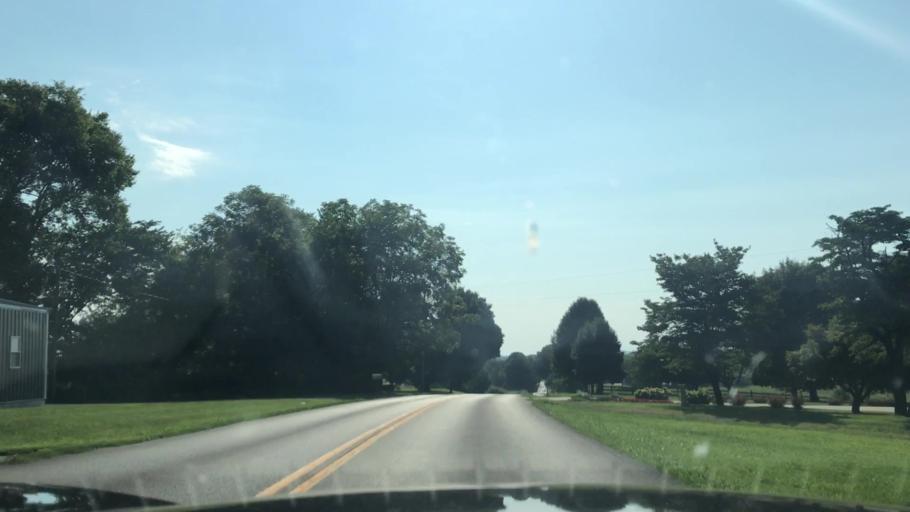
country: US
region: Kentucky
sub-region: Hart County
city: Horse Cave
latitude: 37.1678
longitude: -85.8197
